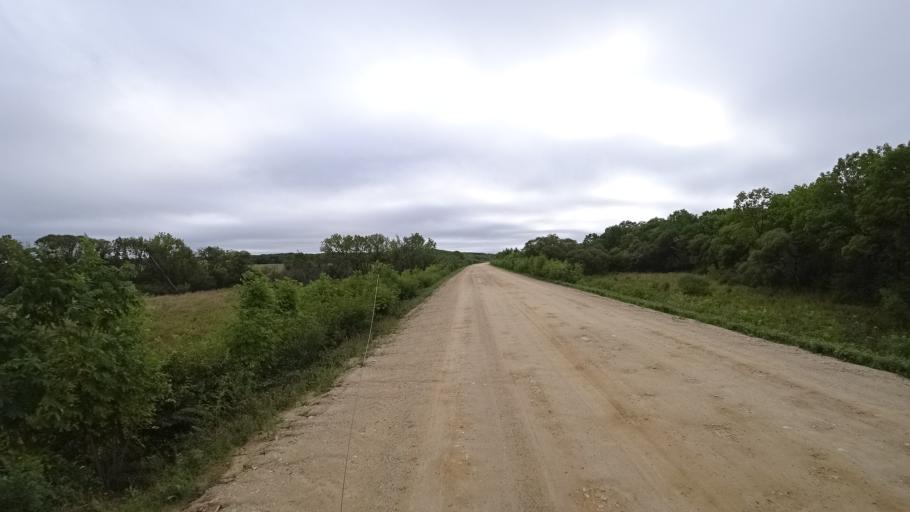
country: RU
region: Primorskiy
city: Rettikhovka
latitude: 44.1241
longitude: 132.6381
